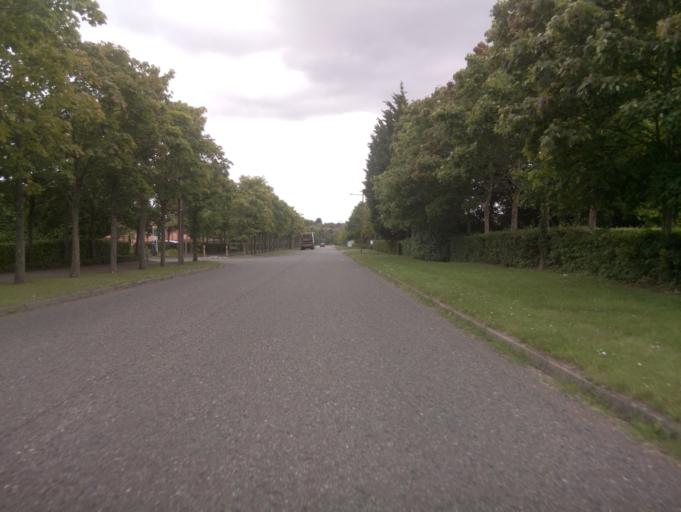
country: GB
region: England
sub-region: Milton Keynes
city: Shenley Church End
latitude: 52.0289
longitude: -0.8000
